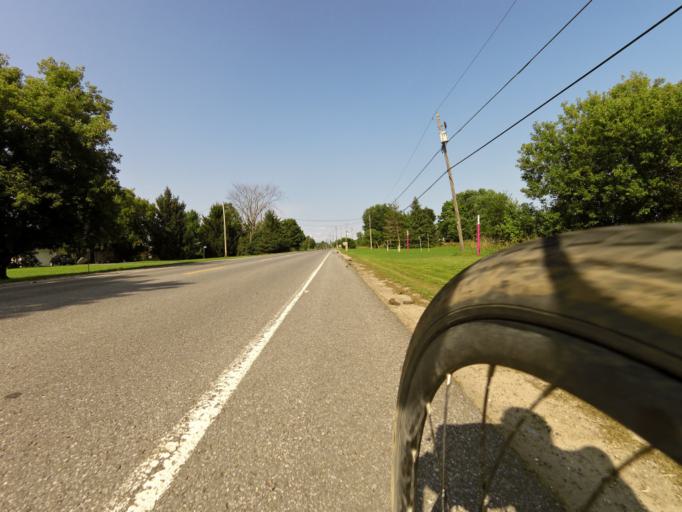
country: CA
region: Ontario
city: Kingston
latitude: 44.2958
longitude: -76.7023
